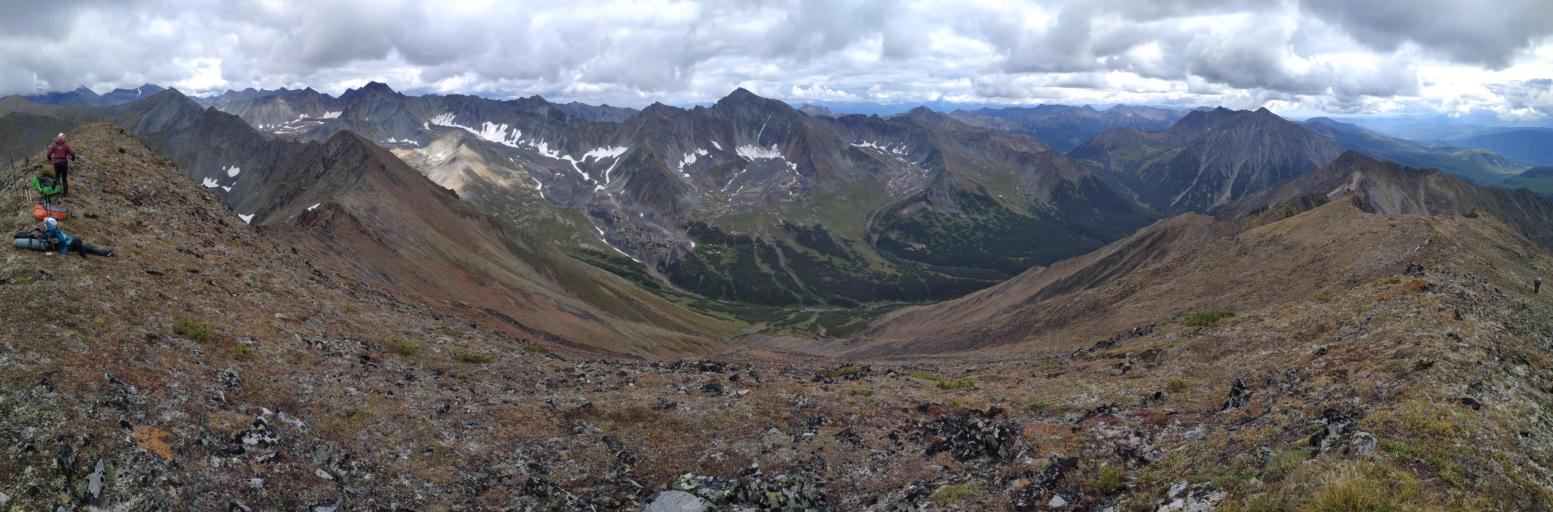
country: RU
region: Kamtsjatka
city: Yelizovo
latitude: 53.8392
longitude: 158.1805
